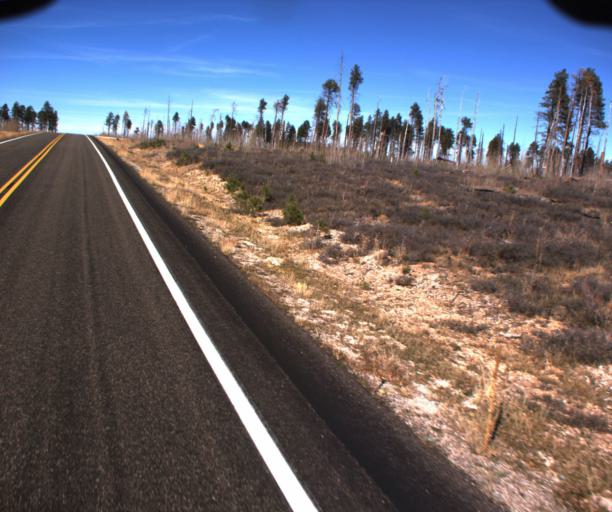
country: US
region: Arizona
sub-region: Coconino County
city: Fredonia
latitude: 36.5984
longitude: -112.1790
